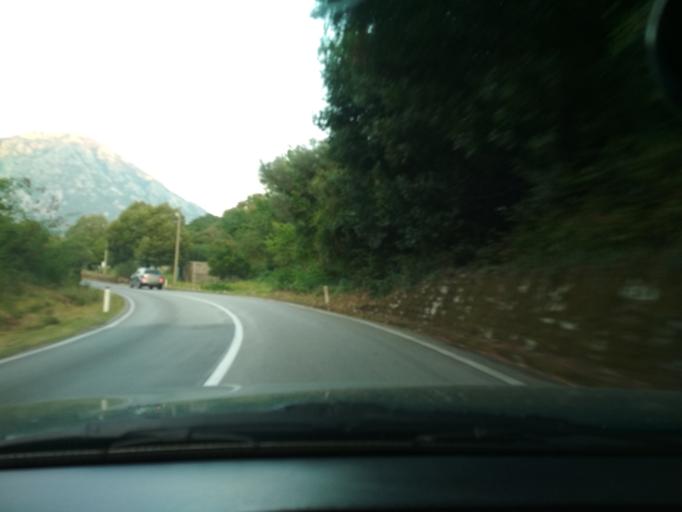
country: ME
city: Lipci
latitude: 42.4868
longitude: 18.6595
